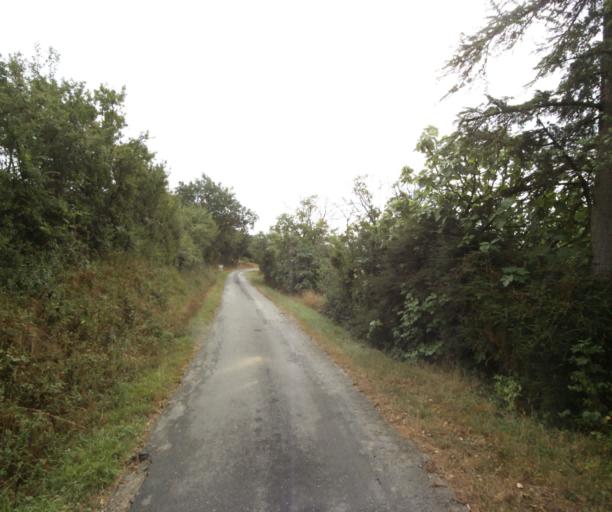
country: FR
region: Midi-Pyrenees
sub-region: Departement de la Haute-Garonne
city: Revel
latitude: 43.4250
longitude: 1.9843
